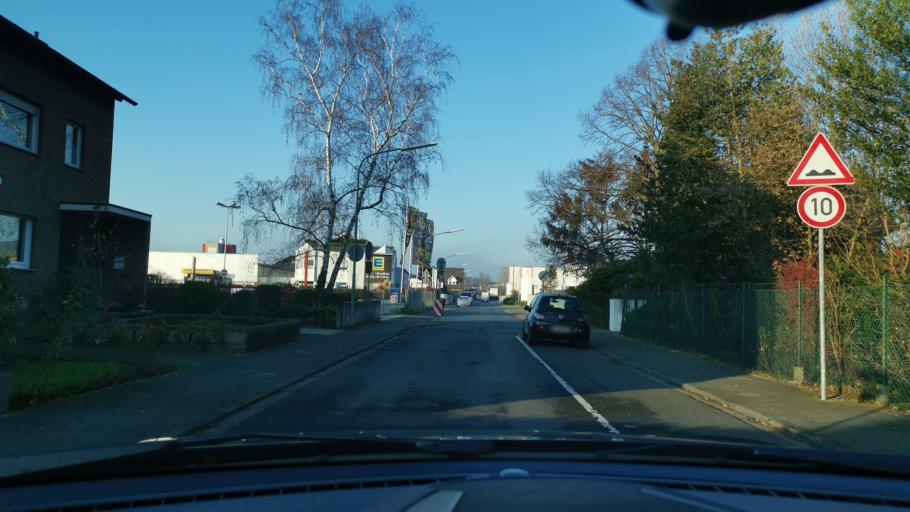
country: DE
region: North Rhine-Westphalia
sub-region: Regierungsbezirk Dusseldorf
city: Neuss
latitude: 51.1462
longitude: 6.7040
